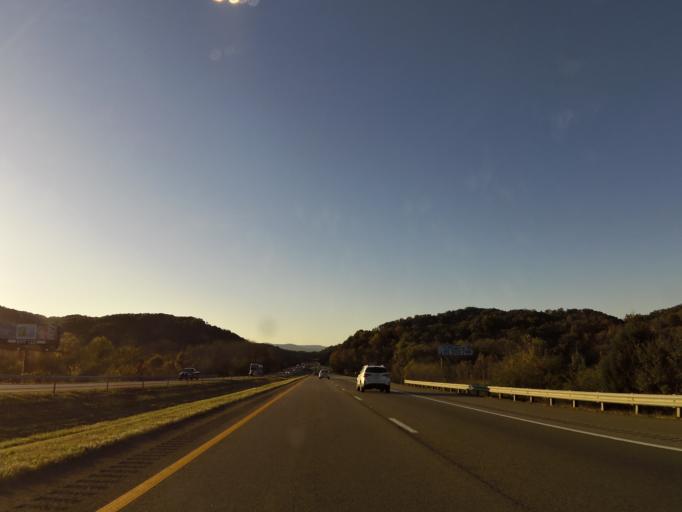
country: US
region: Tennessee
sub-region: Anderson County
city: Norris
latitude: 36.1400
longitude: -84.0450
